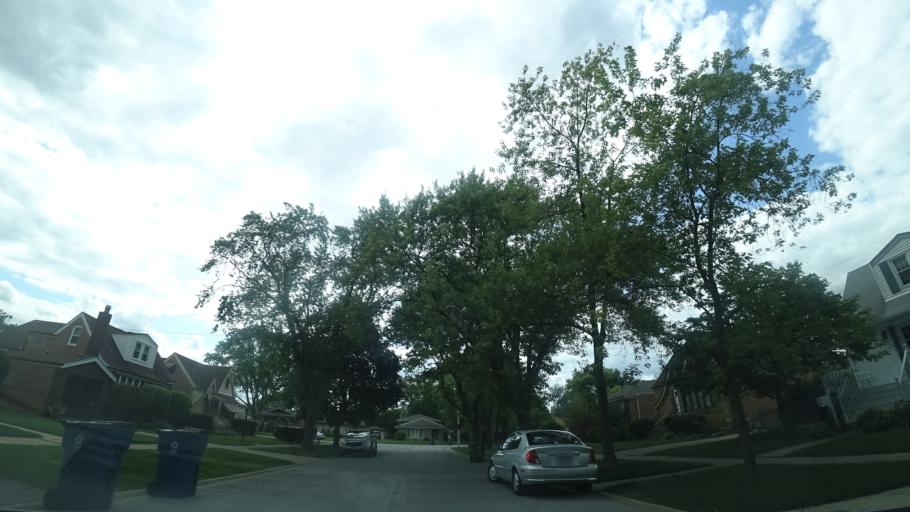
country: US
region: Illinois
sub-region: Cook County
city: Alsip
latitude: 41.6948
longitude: -87.7294
